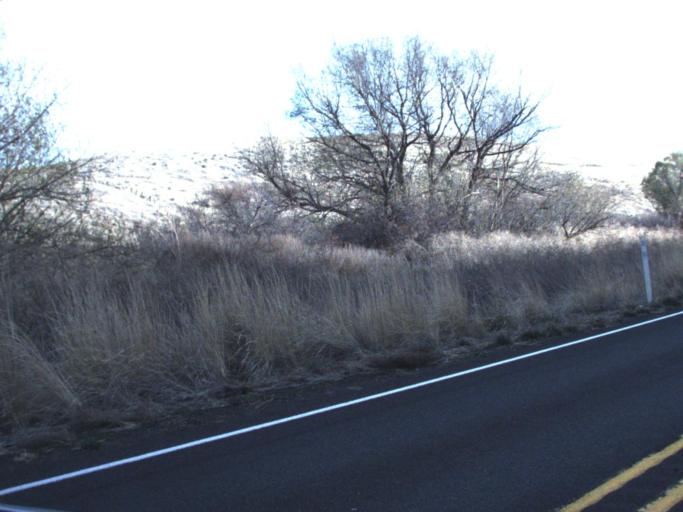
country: US
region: Washington
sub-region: Columbia County
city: Dayton
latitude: 46.4420
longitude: -117.9536
